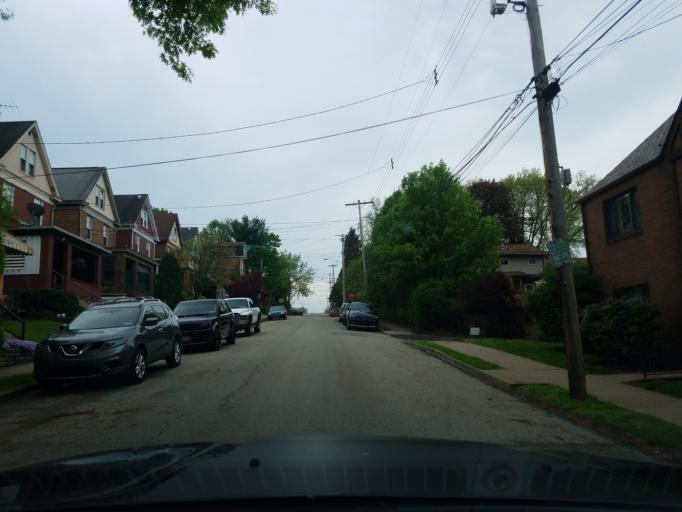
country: US
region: Pennsylvania
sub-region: Allegheny County
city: Swissvale
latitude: 40.4247
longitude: -79.8807
